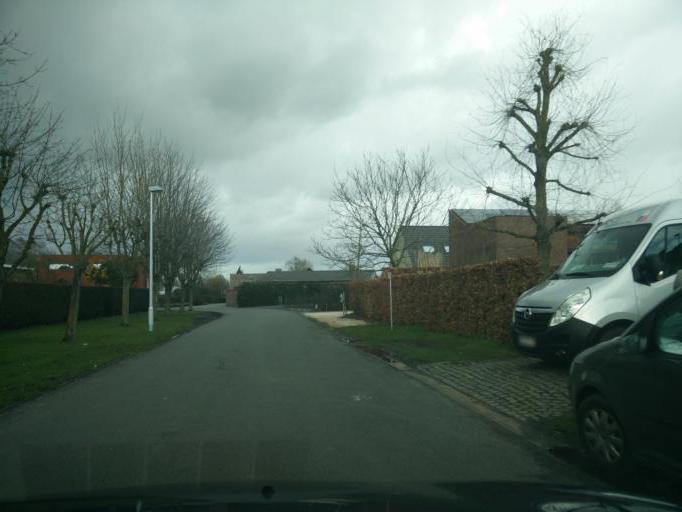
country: BE
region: Flanders
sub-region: Provincie Oost-Vlaanderen
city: Laarne
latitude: 51.0338
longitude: 3.8301
